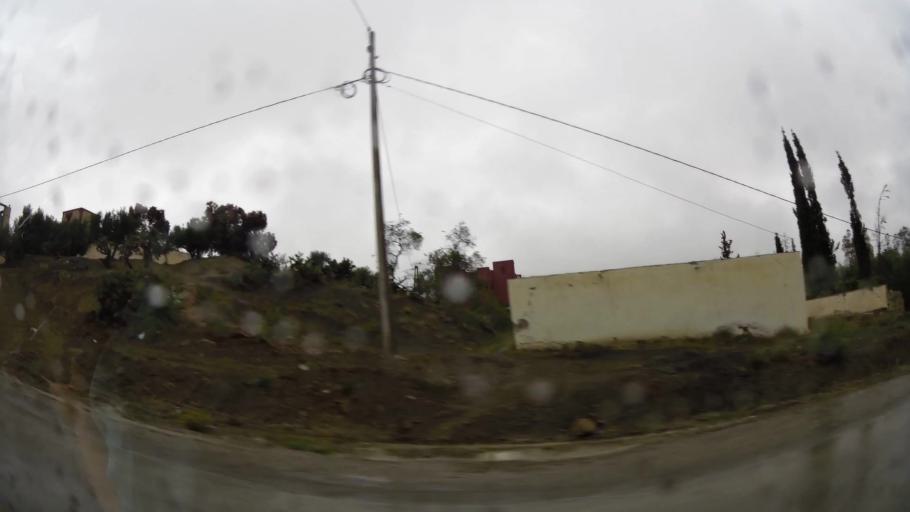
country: MA
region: Taza-Al Hoceima-Taounate
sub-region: Taza
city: Aknoul
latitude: 34.8054
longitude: -3.7379
